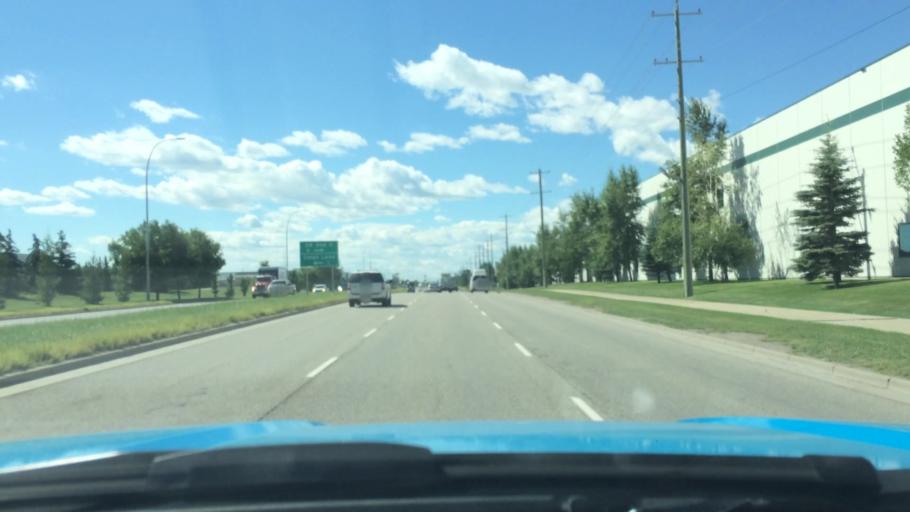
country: CA
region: Alberta
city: Calgary
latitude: 50.9966
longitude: -113.9587
